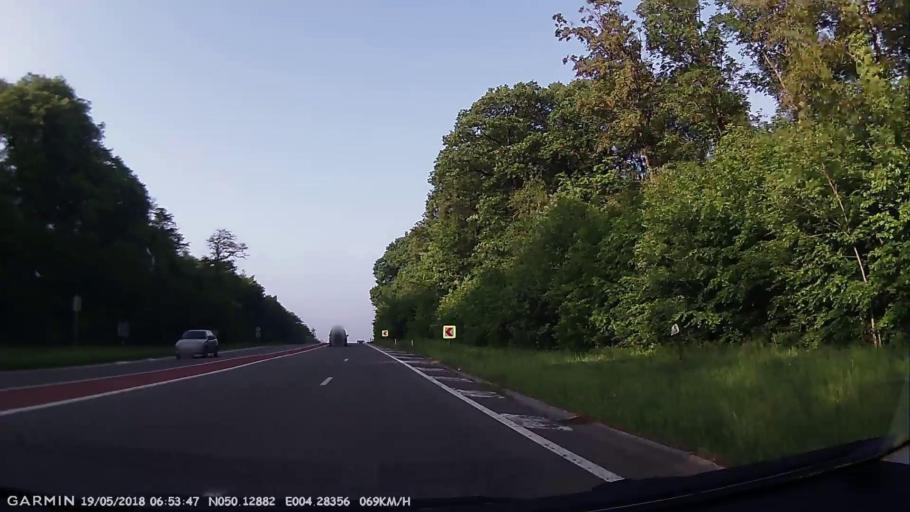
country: BE
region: Wallonia
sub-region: Province du Hainaut
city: Froidchapelle
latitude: 50.1287
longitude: 4.2835
